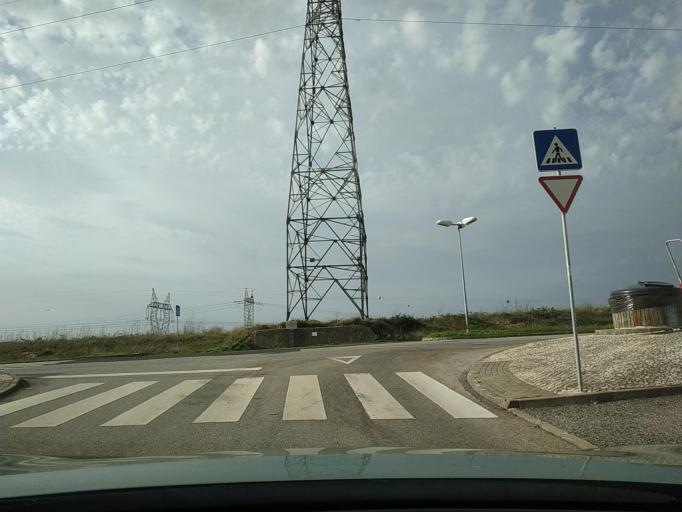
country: PT
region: Lisbon
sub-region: Odivelas
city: Famoes
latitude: 38.7836
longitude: -9.2337
